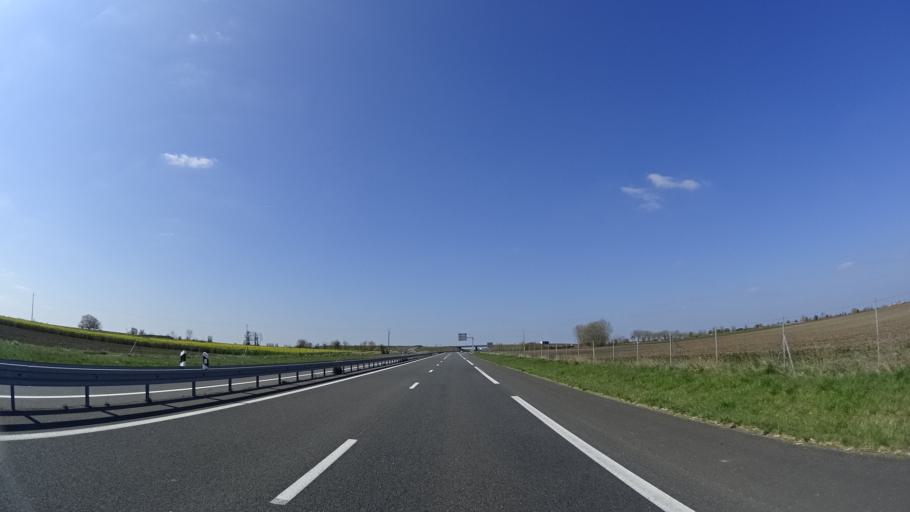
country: FR
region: Pays de la Loire
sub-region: Departement de Maine-et-Loire
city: Saint-Jean
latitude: 47.2860
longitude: -0.3657
